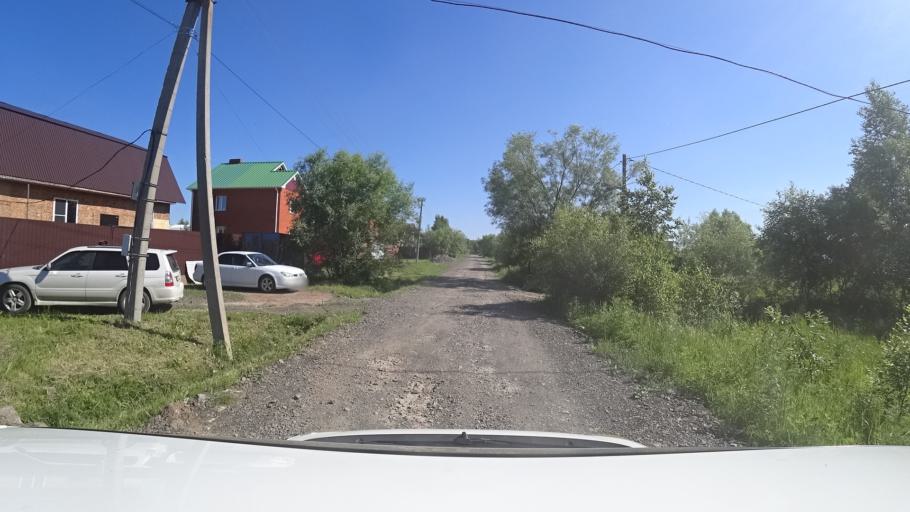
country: RU
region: Khabarovsk Krai
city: Topolevo
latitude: 48.5523
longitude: 135.1690
